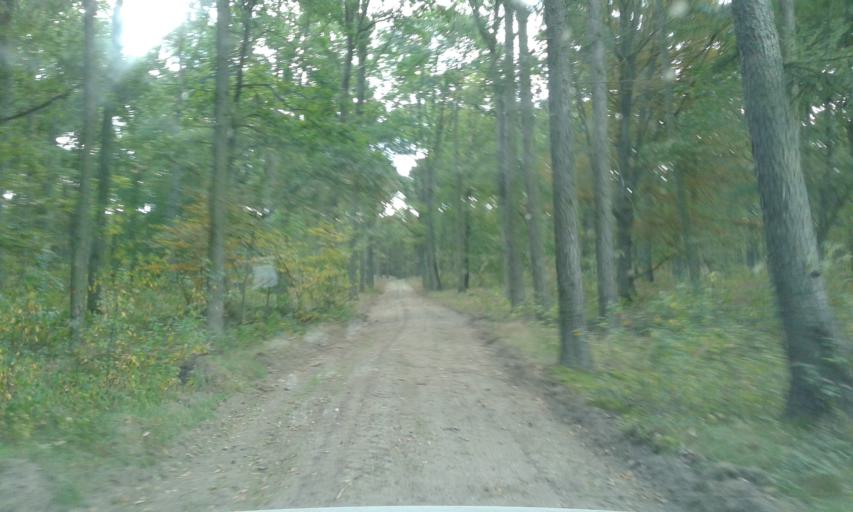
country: PL
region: West Pomeranian Voivodeship
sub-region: Powiat stargardzki
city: Dolice
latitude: 53.2327
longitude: 15.2451
